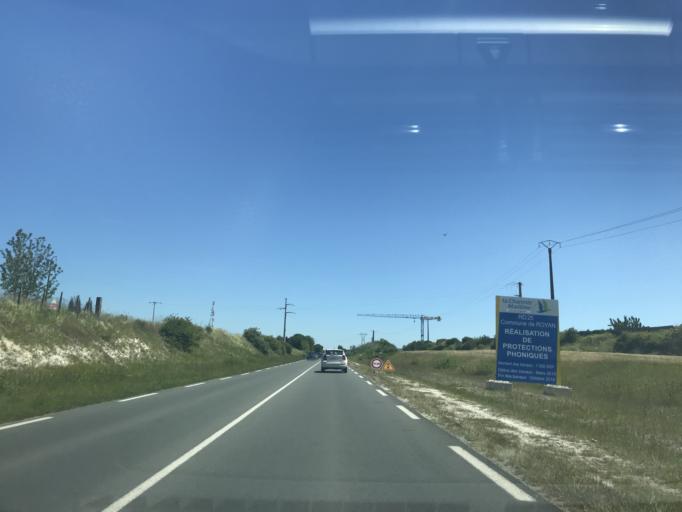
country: FR
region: Poitou-Charentes
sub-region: Departement de la Charente-Maritime
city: Vaux-sur-Mer
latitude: 45.6434
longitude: -1.0402
